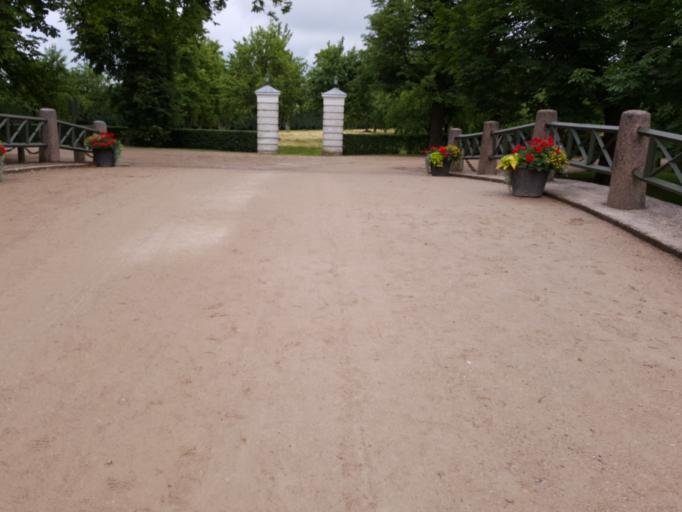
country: LV
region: Rundales
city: Pilsrundale
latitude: 56.4144
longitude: 24.0259
